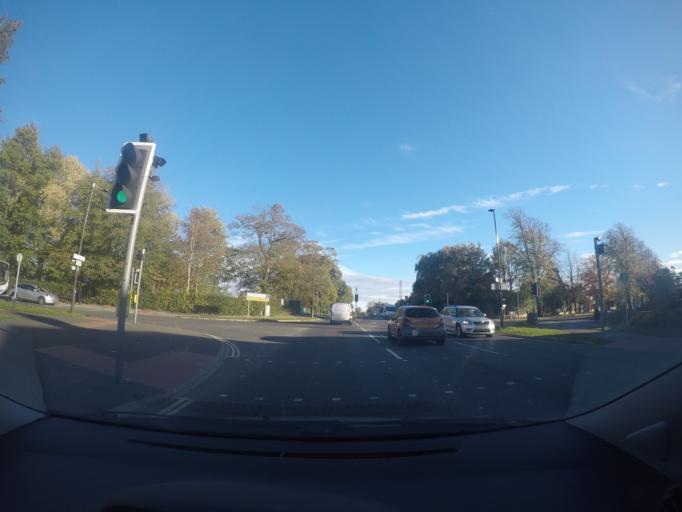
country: GB
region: England
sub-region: City of York
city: Nether Poppleton
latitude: 53.9701
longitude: -1.1338
